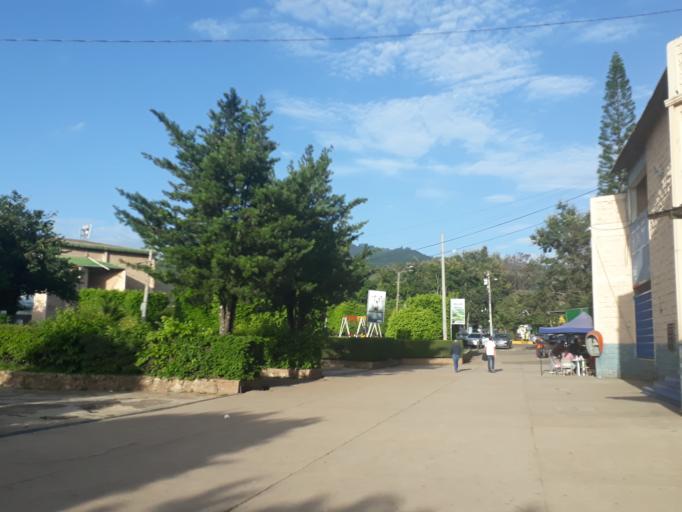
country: HN
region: Francisco Morazan
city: Tegucigalpa
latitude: 14.0903
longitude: -87.1632
